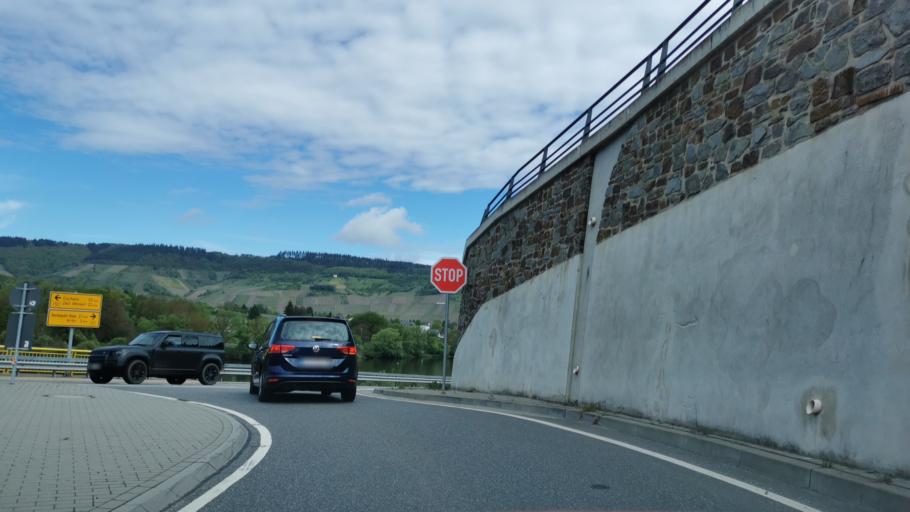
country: DE
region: Rheinland-Pfalz
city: Enkirch
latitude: 49.9681
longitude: 7.1055
